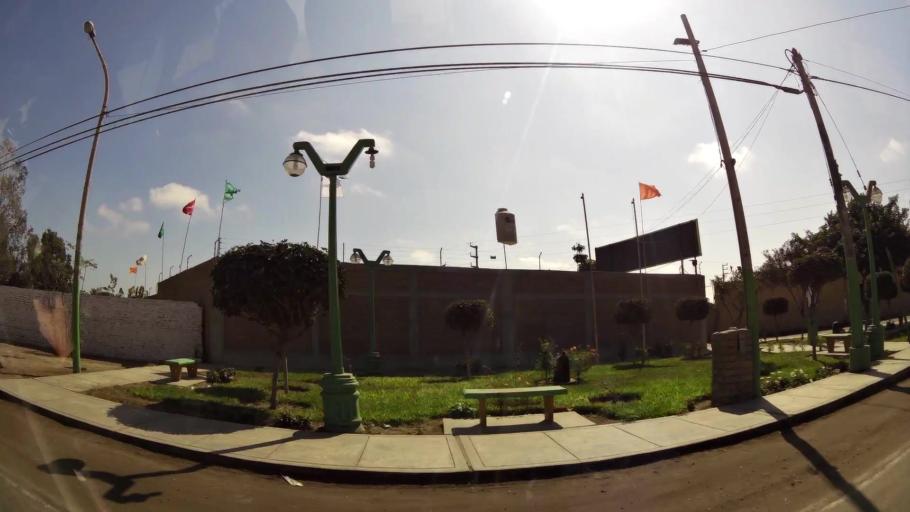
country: PE
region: Ica
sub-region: Provincia de Chincha
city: Sunampe
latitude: -13.4176
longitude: -76.1574
